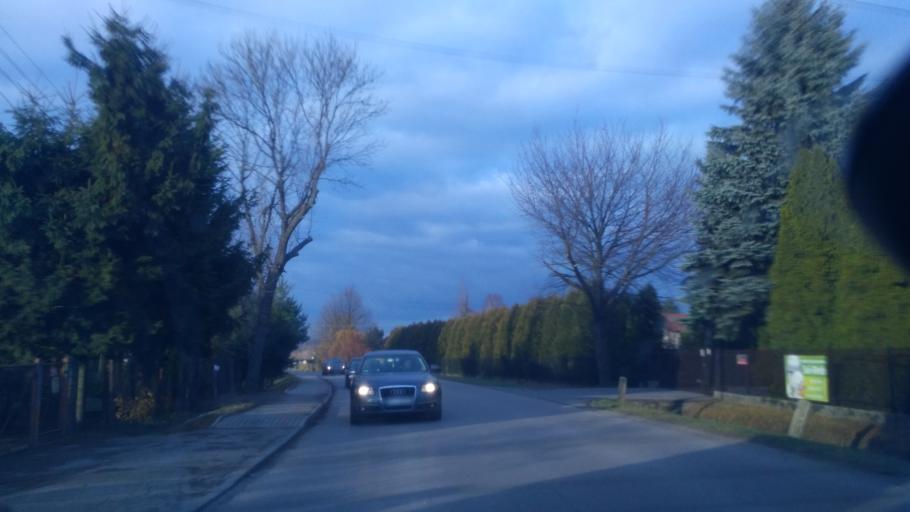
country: PL
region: Subcarpathian Voivodeship
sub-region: Powiat rzeszowski
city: Krasne
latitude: 50.0586
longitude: 22.1199
